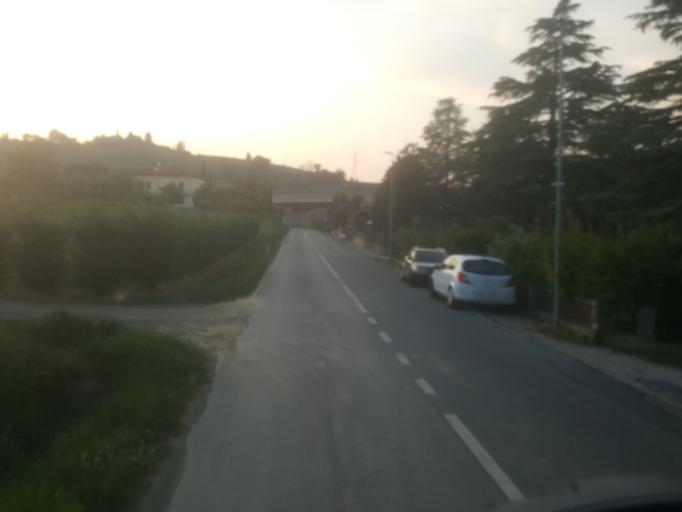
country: IT
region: Tuscany
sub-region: Province of Florence
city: Certaldo
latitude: 43.5313
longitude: 11.0363
